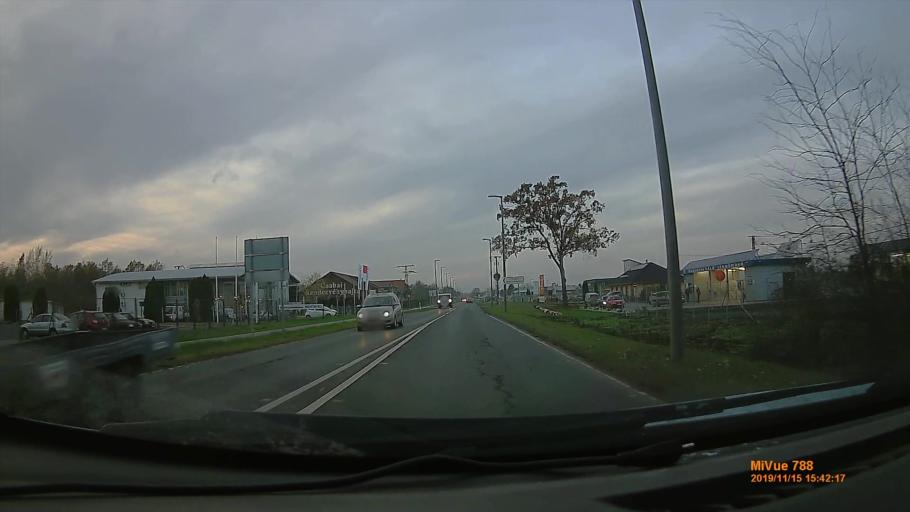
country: HU
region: Bekes
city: Bekescsaba
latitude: 46.6773
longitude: 21.1272
